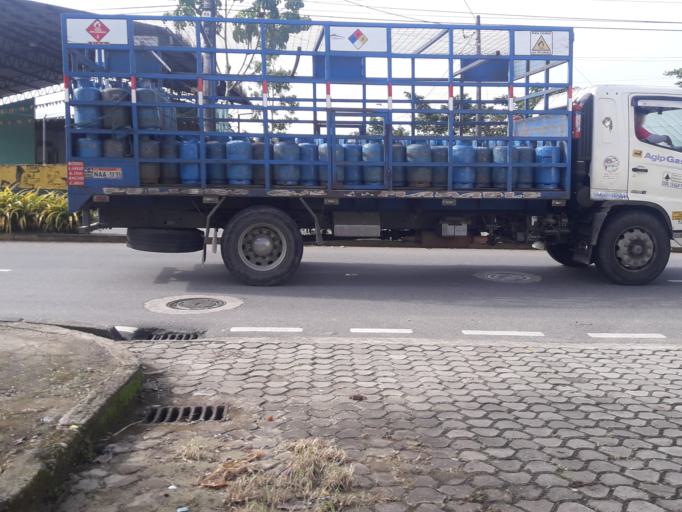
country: EC
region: Napo
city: Tena
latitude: -0.9836
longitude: -77.8110
